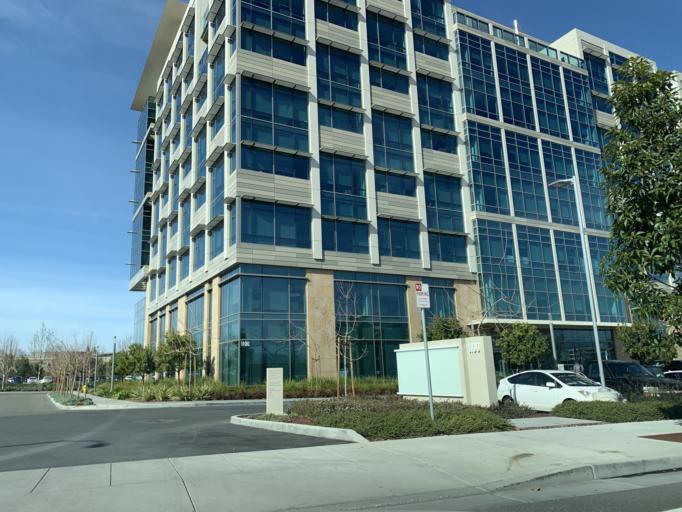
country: US
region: California
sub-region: Santa Clara County
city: Sunnyvale
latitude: 37.4061
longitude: -122.0334
